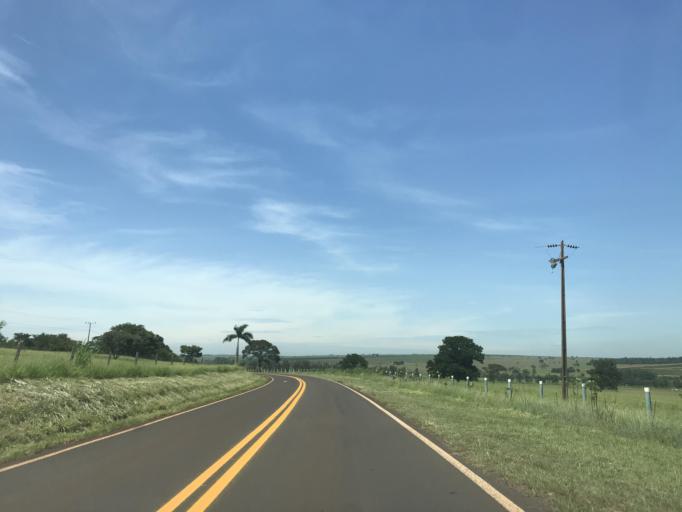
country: BR
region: Parana
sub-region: Terra Rica
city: Terra Rica
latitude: -22.7799
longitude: -52.6573
